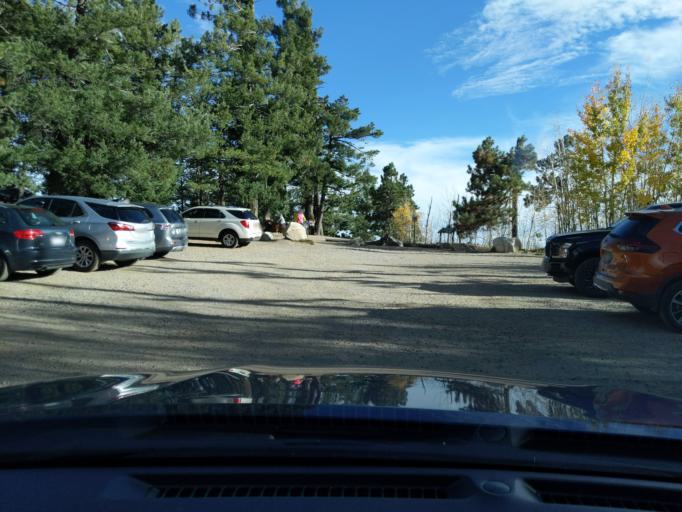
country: US
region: Arizona
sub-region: Pima County
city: Catalina
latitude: 32.4406
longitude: -110.7859
